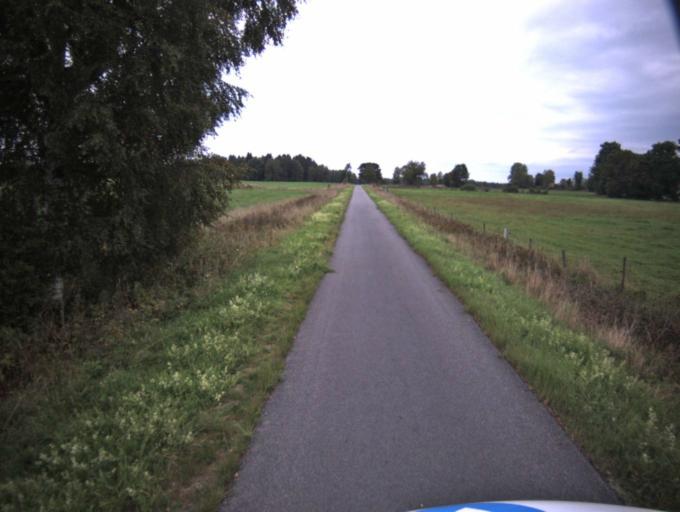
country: SE
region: Vaestra Goetaland
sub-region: Ulricehamns Kommun
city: Ulricehamn
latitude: 57.9655
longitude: 13.5152
